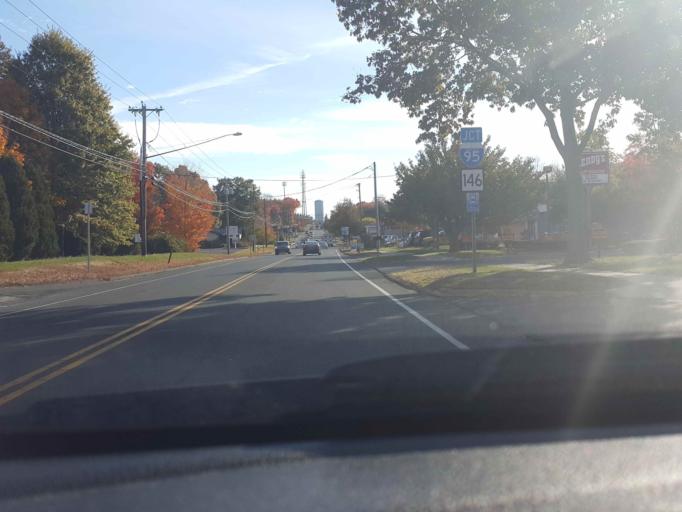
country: US
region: Connecticut
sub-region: New Haven County
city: Guilford Center
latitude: 41.2887
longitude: -72.6677
